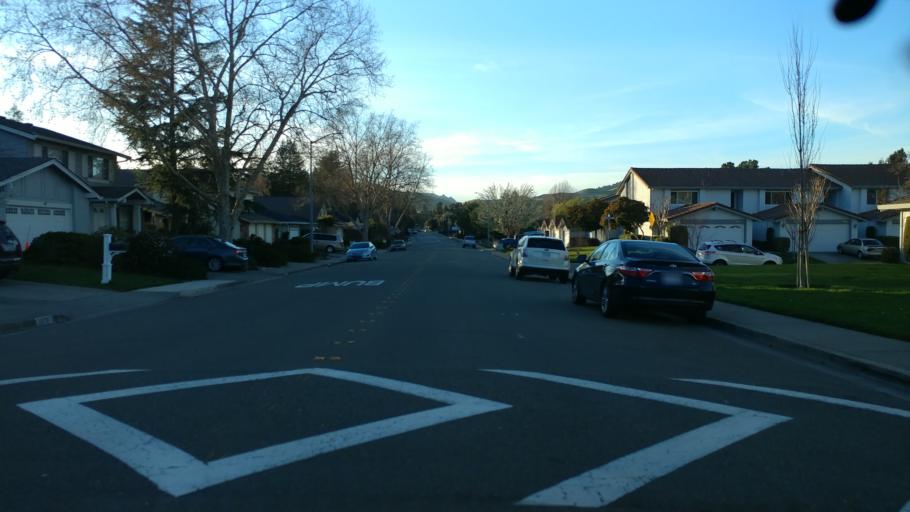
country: US
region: California
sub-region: Contra Costa County
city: San Ramon
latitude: 37.7664
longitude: -121.9783
